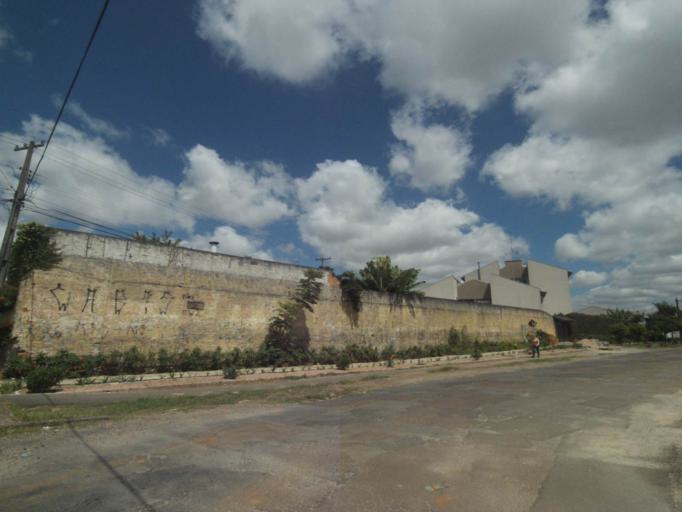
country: BR
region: Parana
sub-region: Pinhais
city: Pinhais
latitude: -25.4429
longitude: -49.2039
